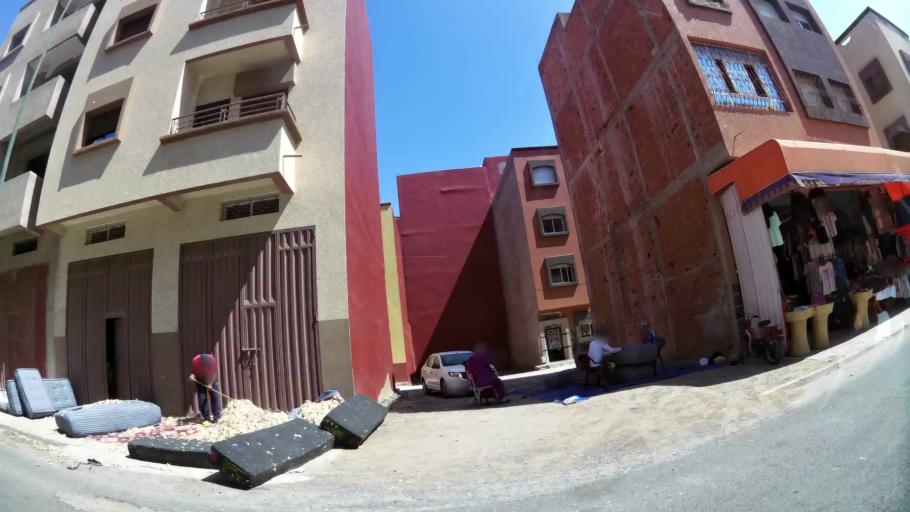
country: MA
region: Gharb-Chrarda-Beni Hssen
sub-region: Kenitra Province
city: Kenitra
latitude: 34.2386
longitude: -6.5526
